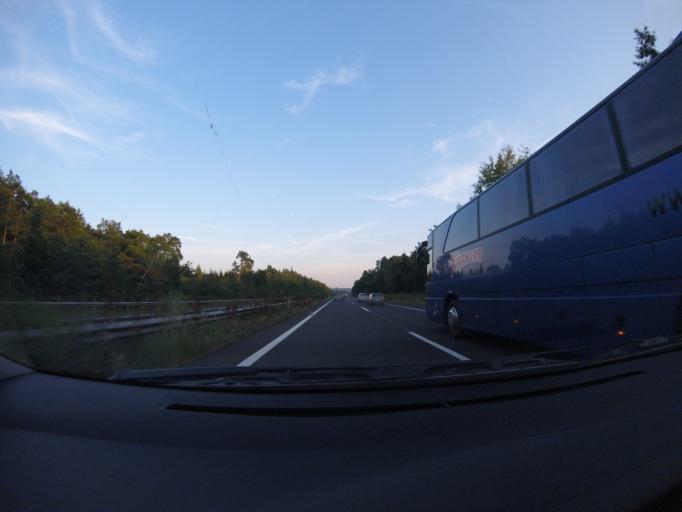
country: AT
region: Styria
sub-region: Politischer Bezirk Hartberg-Fuerstenfeld
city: Hainersdorf
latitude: 47.1100
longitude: 15.9848
